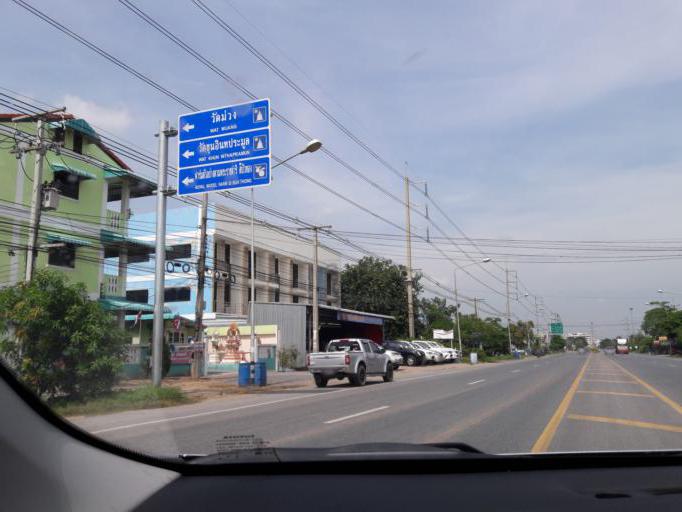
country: TH
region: Ang Thong
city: Ang Thong
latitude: 14.5732
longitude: 100.4540
